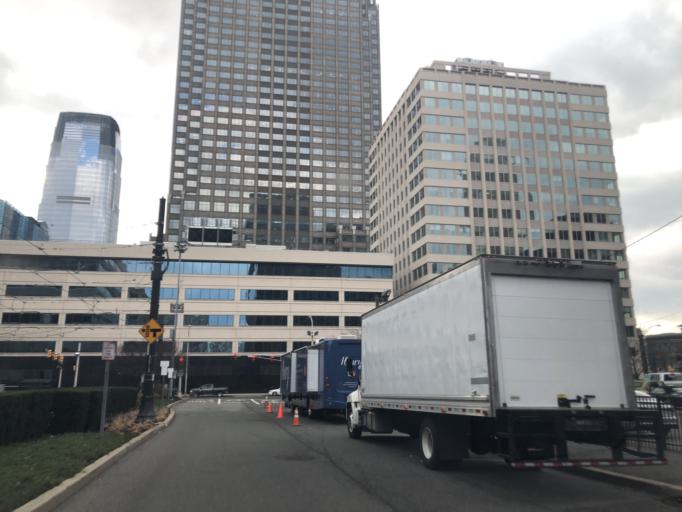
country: US
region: New Jersey
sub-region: Hudson County
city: Hoboken
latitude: 40.7180
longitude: -74.0345
